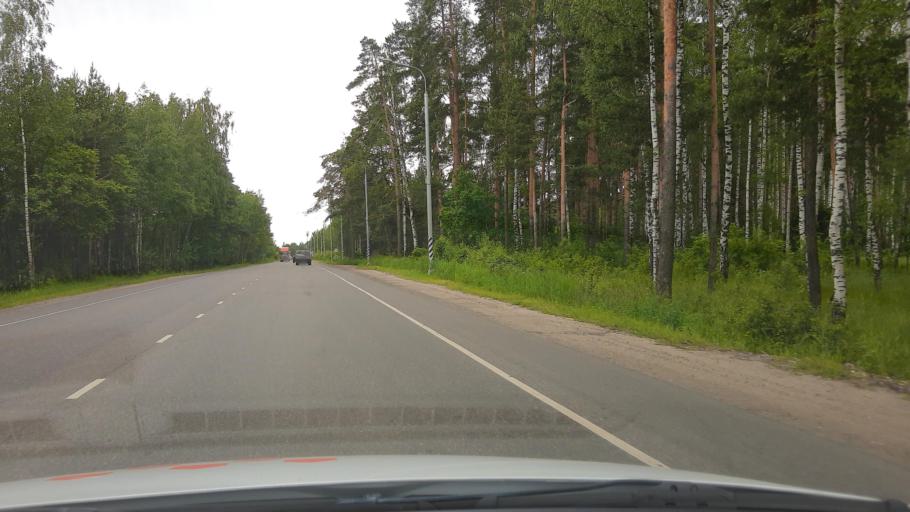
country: RU
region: Moskovskaya
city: Noginsk
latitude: 55.8609
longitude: 38.4107
